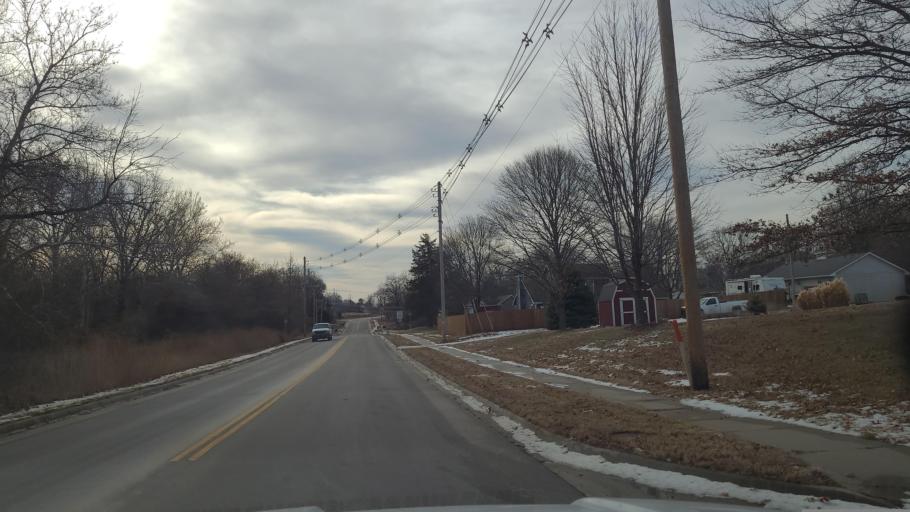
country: US
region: Kansas
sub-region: Douglas County
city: Baldwin City
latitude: 38.7708
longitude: -95.1862
